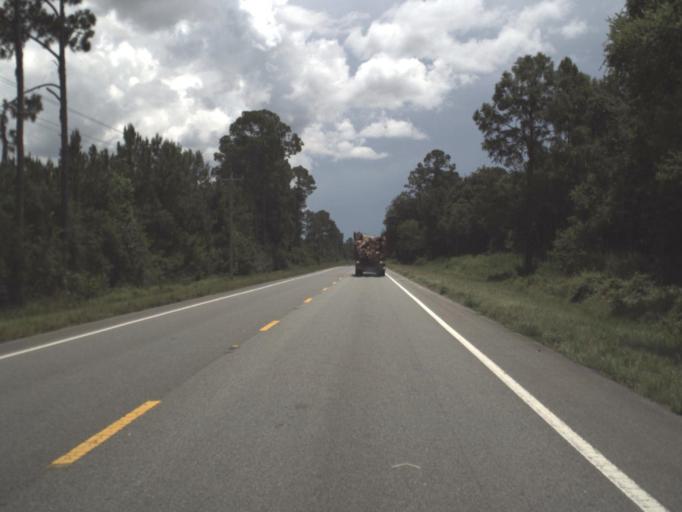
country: US
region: Florida
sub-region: Taylor County
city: Perry
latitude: 30.0906
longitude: -83.6783
